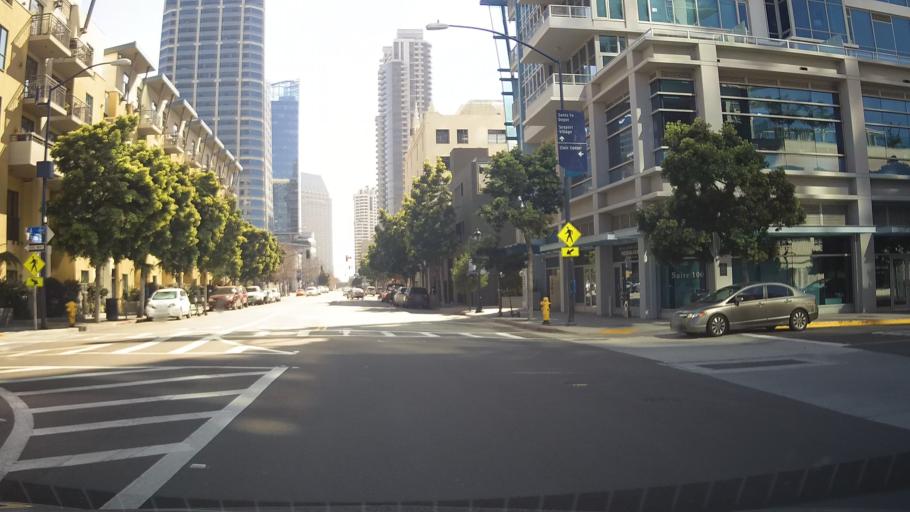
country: US
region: California
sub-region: San Diego County
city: San Diego
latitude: 32.7190
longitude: -117.1692
